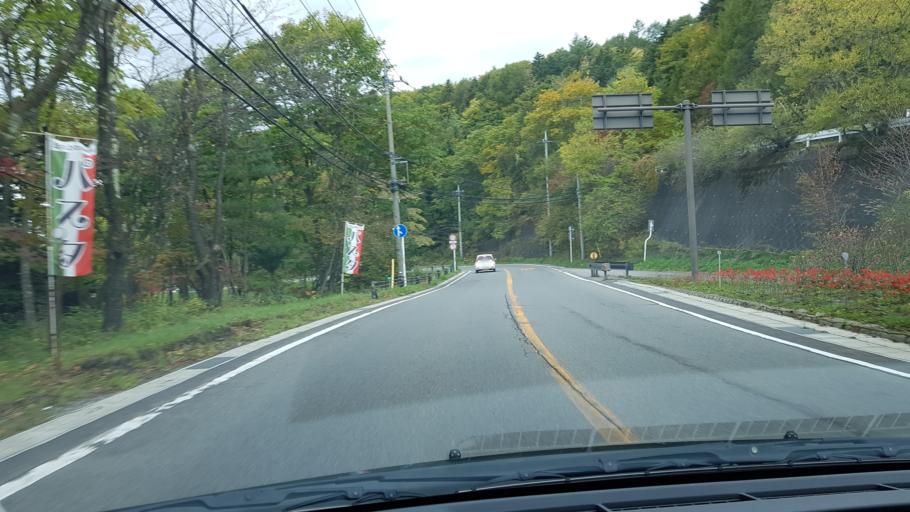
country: JP
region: Gunma
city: Nakanojomachi
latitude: 36.6078
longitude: 138.5843
